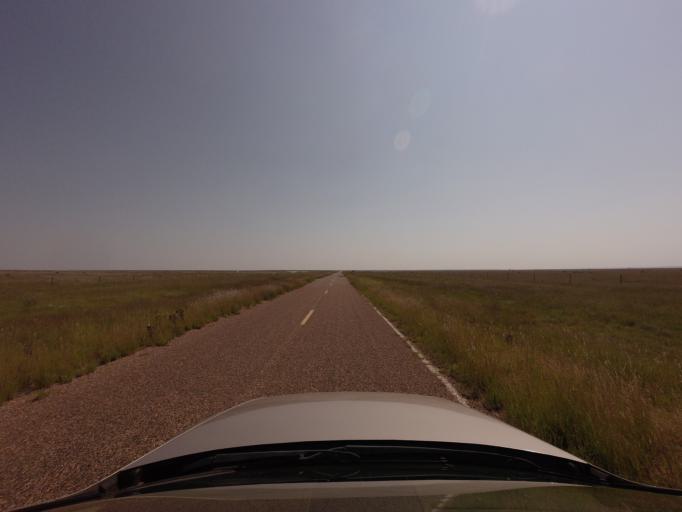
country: US
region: New Mexico
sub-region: Curry County
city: Cannon Air Force Base
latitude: 34.6332
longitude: -103.4273
